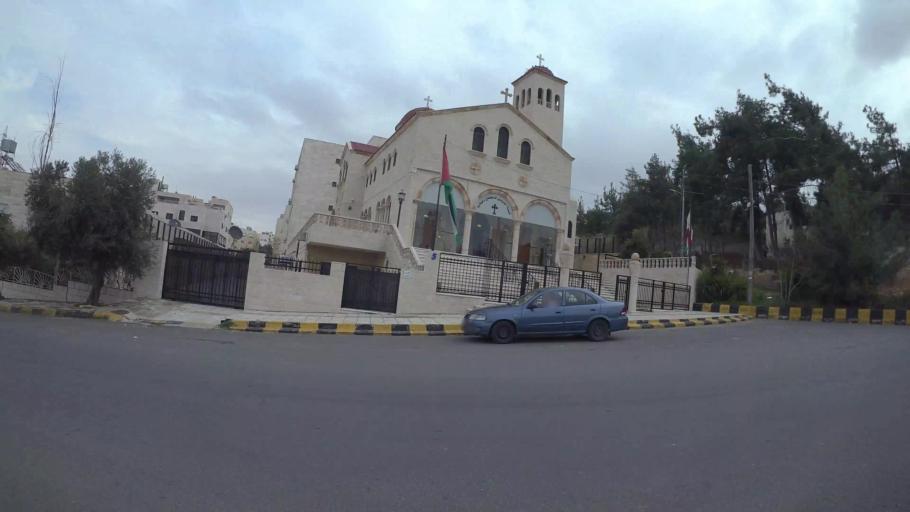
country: JO
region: Amman
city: Umm as Summaq
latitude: 31.8972
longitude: 35.8600
